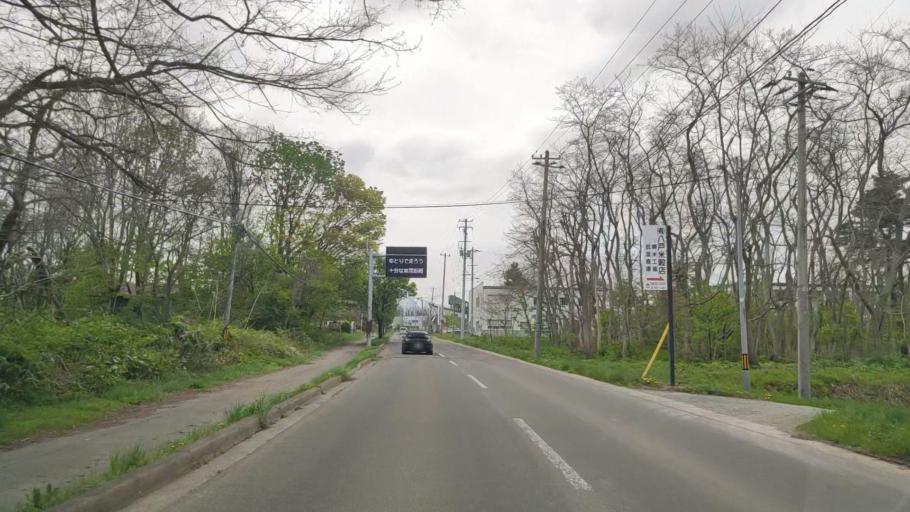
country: JP
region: Aomori
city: Aomori Shi
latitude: 40.7760
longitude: 140.7951
